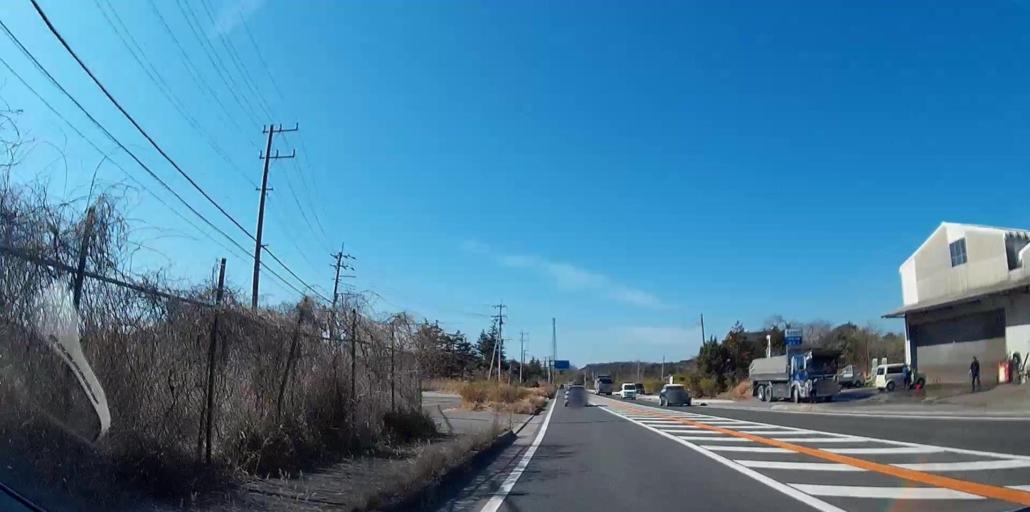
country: JP
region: Chiba
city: Kimitsu
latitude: 35.2350
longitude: 139.8846
